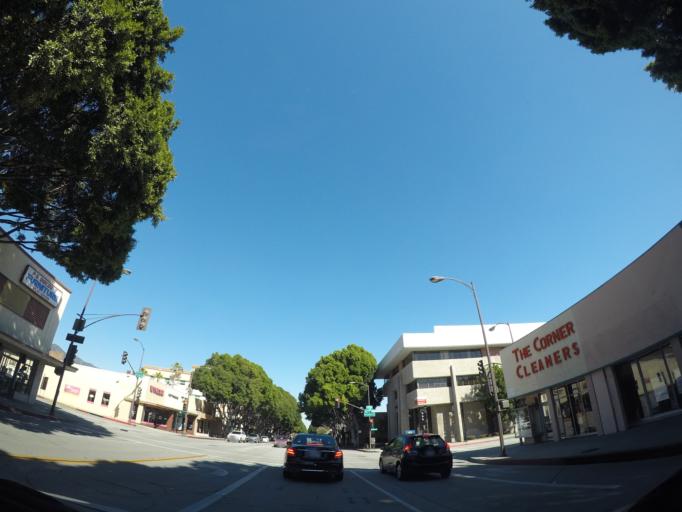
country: US
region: California
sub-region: Los Angeles County
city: East Pasadena
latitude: 34.1461
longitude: -118.0990
